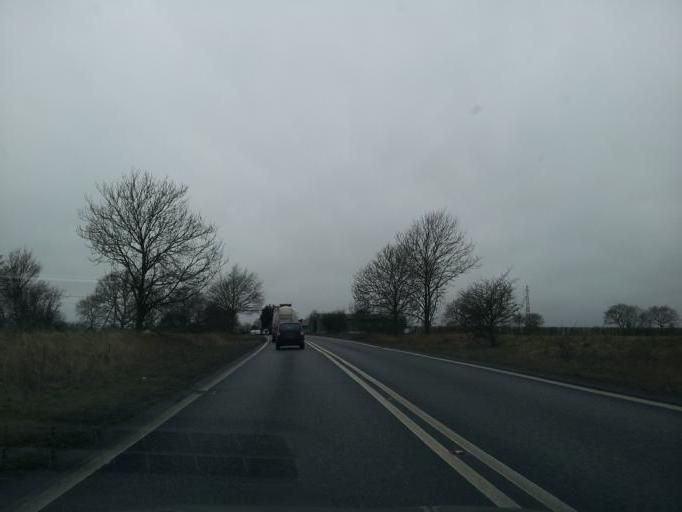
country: GB
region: England
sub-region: Essex
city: Mistley
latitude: 51.9015
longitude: 1.0757
